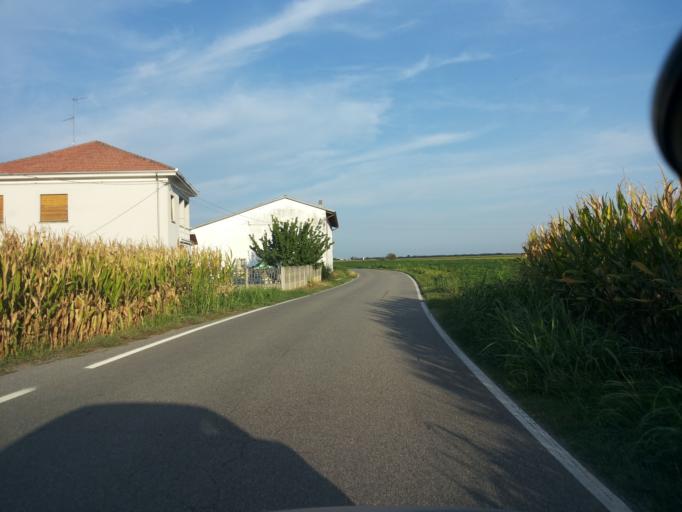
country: IT
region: Piedmont
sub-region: Provincia di Vercelli
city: Tronzano Vercellese
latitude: 45.3388
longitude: 8.1836
